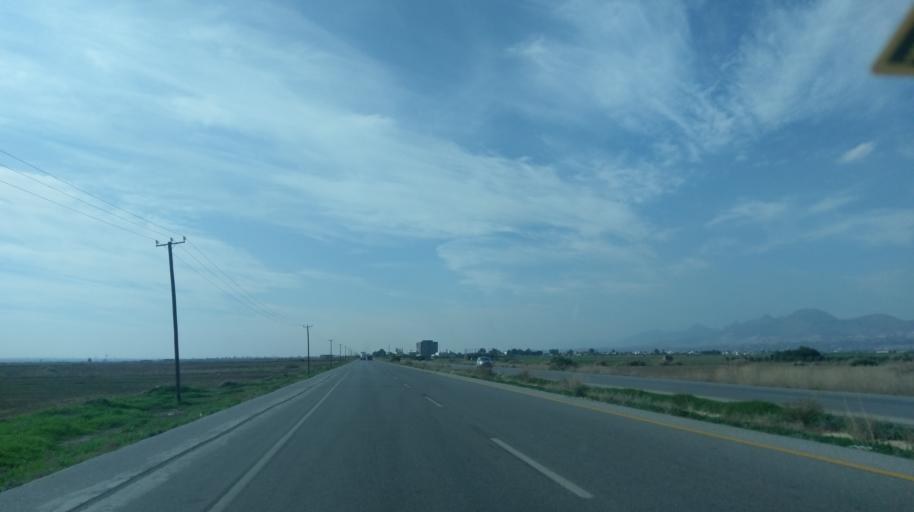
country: CY
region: Larnaka
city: Athienou
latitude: 35.2112
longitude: 33.5444
